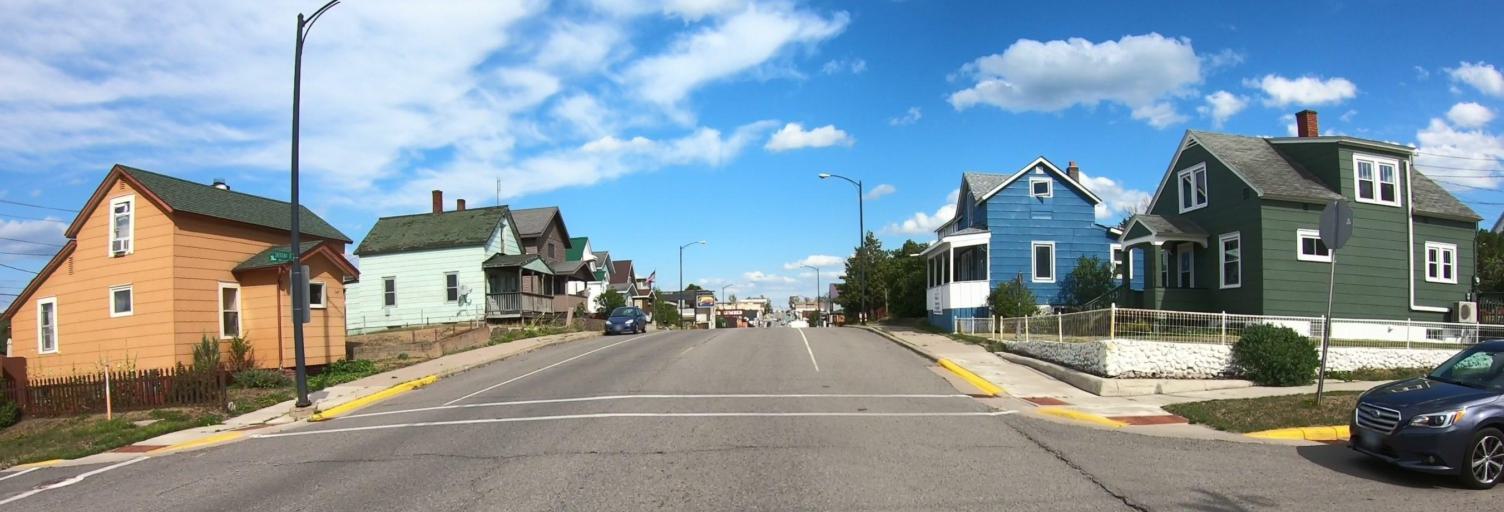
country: US
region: Minnesota
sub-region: Saint Louis County
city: Ely
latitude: 47.9033
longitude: -91.8714
